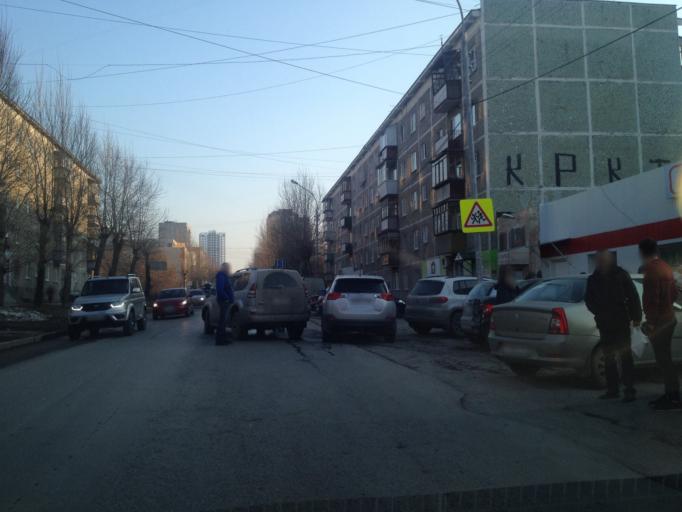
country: RU
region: Sverdlovsk
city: Yekaterinburg
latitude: 56.8304
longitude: 60.5517
